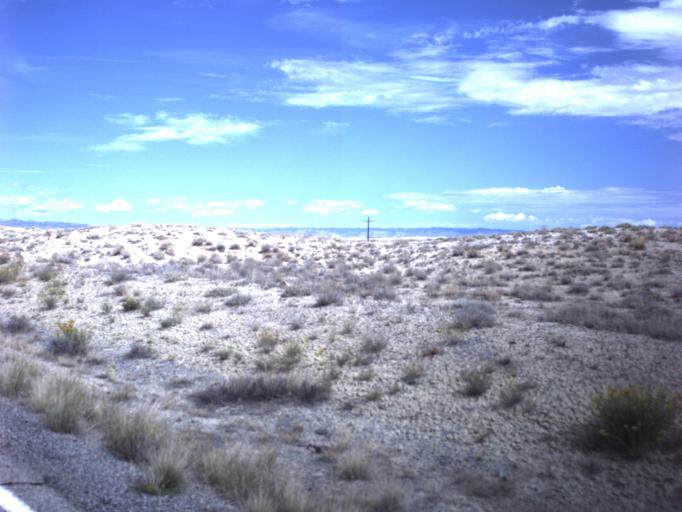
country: US
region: Utah
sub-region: Grand County
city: Moab
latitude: 38.9433
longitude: -109.3527
